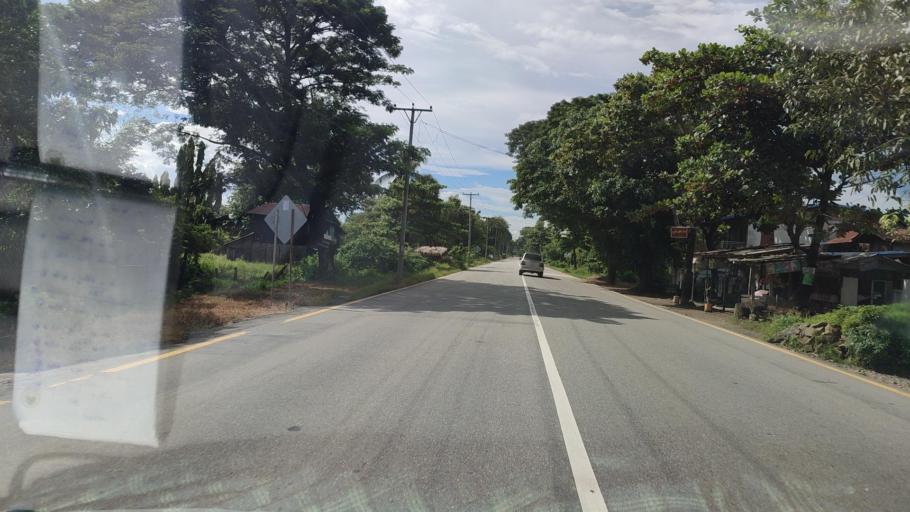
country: MM
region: Bago
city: Pyu
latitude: 18.4464
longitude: 96.4414
